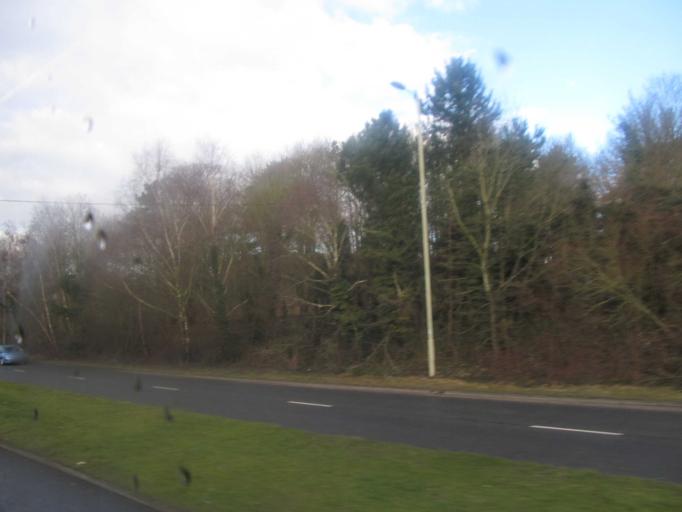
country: GB
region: England
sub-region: Hampshire
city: Basingstoke
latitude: 51.2661
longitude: -1.1049
